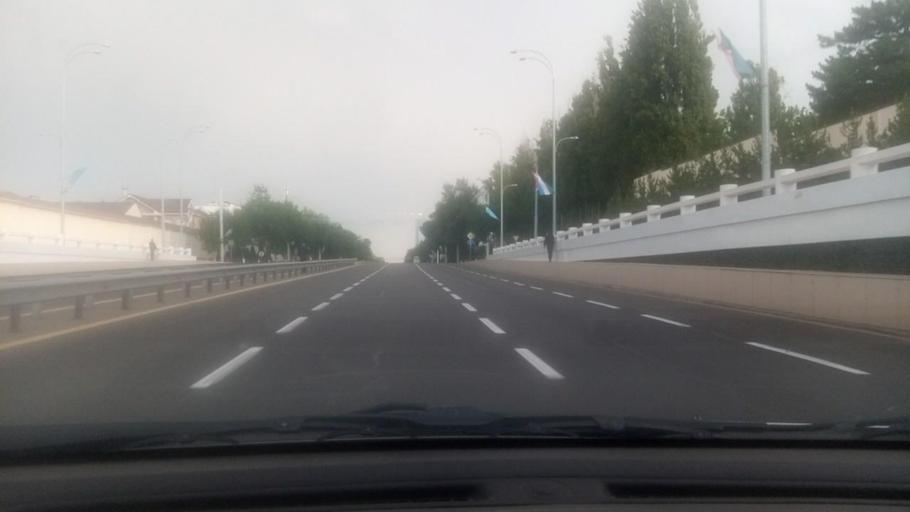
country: UZ
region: Toshkent
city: Salor
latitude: 41.3331
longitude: 69.3485
